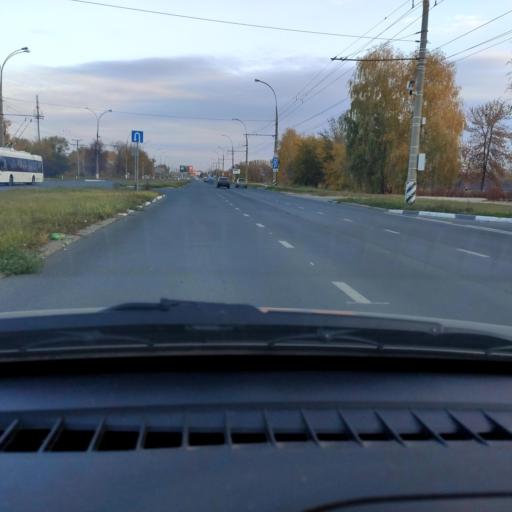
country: RU
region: Samara
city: Tol'yatti
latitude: 53.5431
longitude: 49.3009
